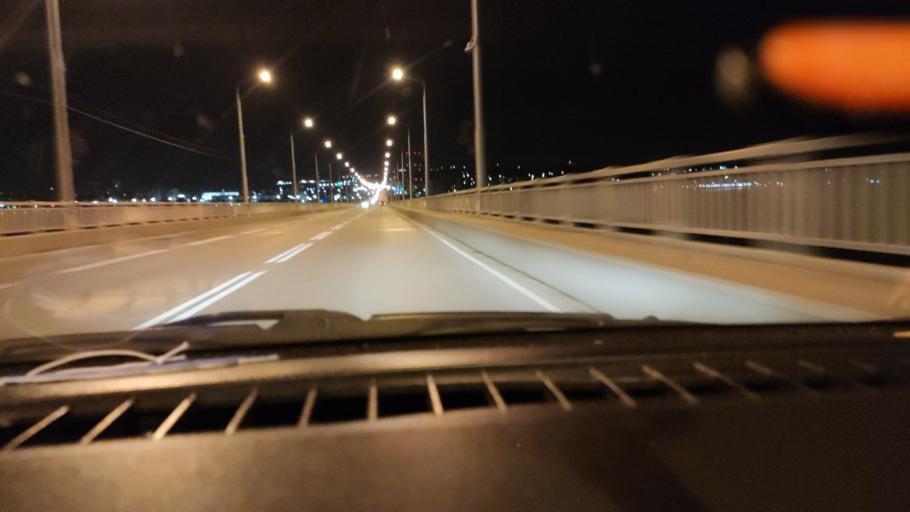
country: RU
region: Saratov
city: Engel's
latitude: 51.5117
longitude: 46.0741
